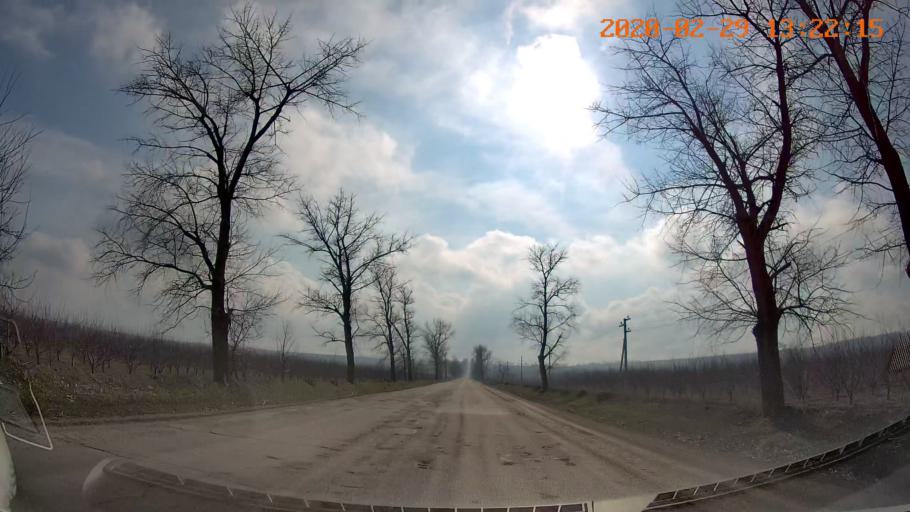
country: MD
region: Telenesti
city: Camenca
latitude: 47.9626
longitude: 28.6283
